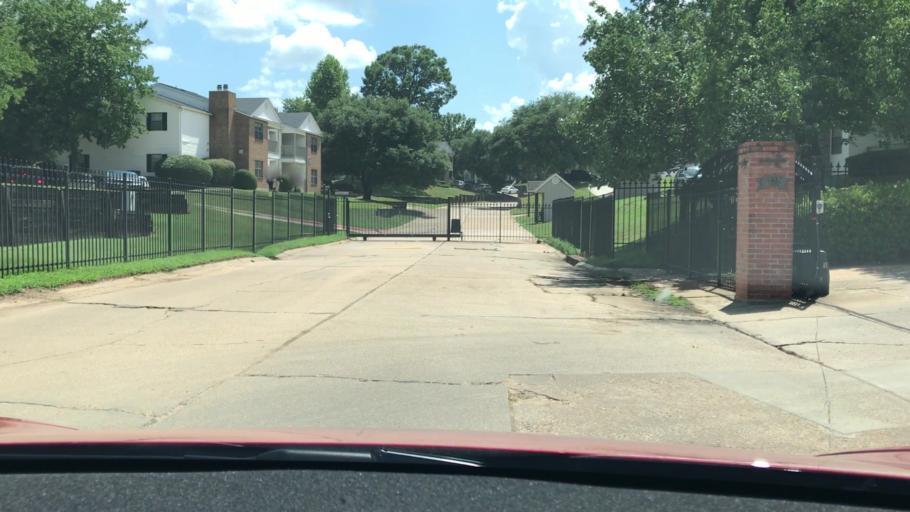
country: US
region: Louisiana
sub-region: Bossier Parish
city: Bossier City
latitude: 32.4200
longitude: -93.7288
